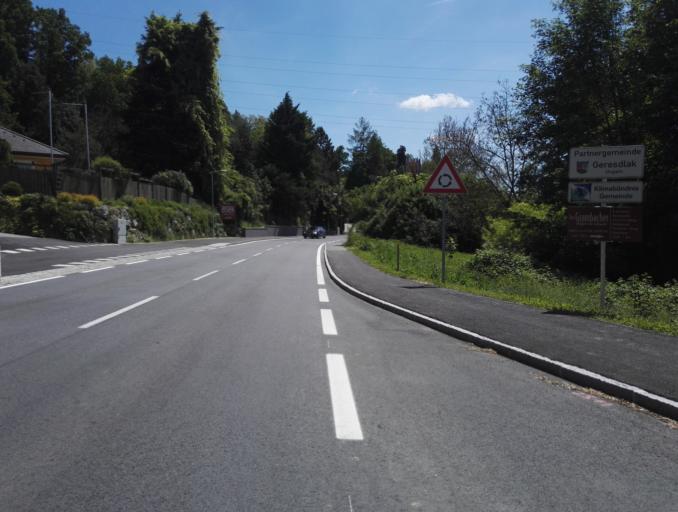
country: AT
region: Styria
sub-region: Politischer Bezirk Graz-Umgebung
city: Grambach
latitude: 47.0201
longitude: 15.5017
